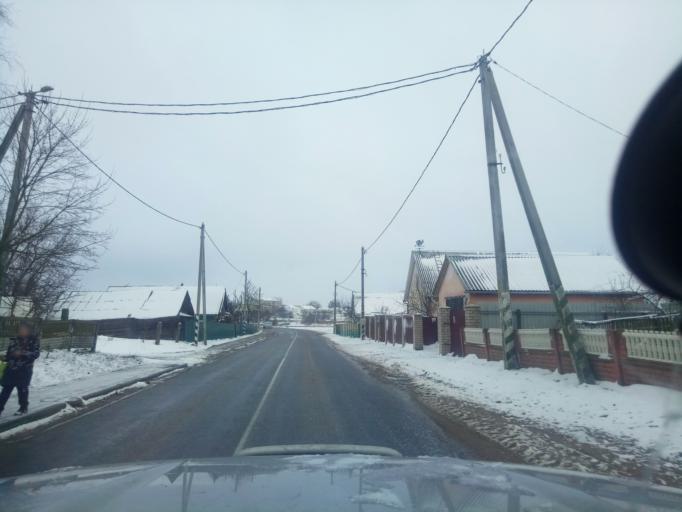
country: BY
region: Minsk
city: Tsimkavichy
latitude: 53.0681
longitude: 26.9883
